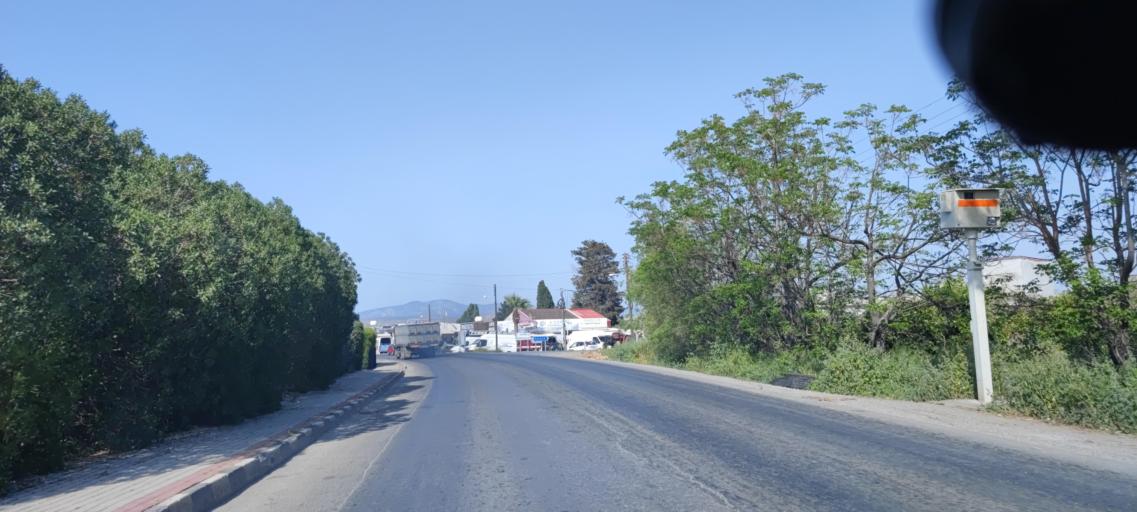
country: CY
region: Lefkosia
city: Morfou
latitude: 35.2072
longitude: 32.9991
